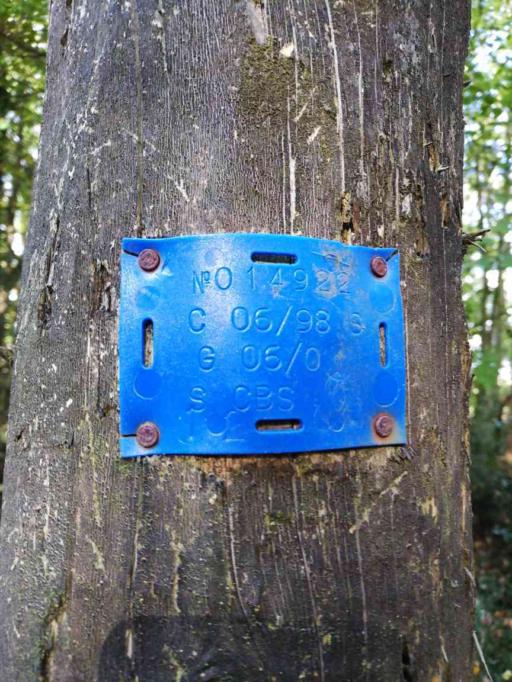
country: FR
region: Pays de la Loire
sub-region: Departement de la Vendee
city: Le Champ-Saint-Pere
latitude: 46.5004
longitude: -1.3456
